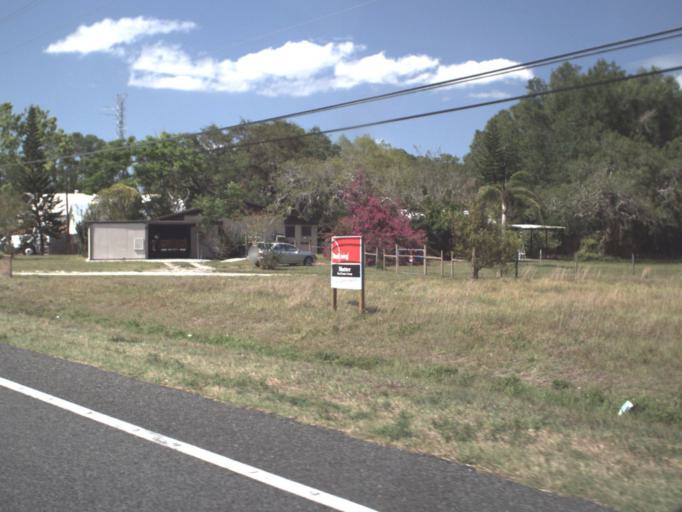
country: US
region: Florida
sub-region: Brevard County
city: Mims
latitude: 28.6812
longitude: -80.8522
